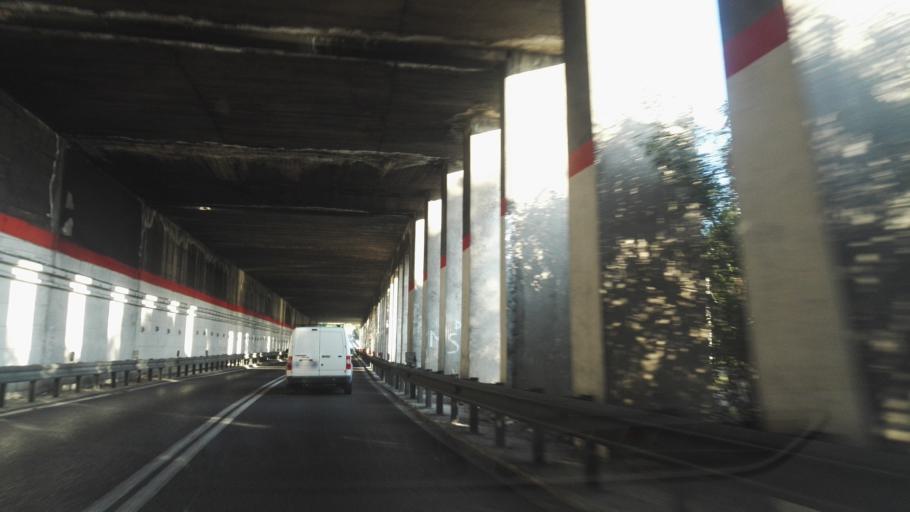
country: IT
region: Calabria
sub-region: Provincia di Catanzaro
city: Squillace Lido
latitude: 38.7651
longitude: 16.5657
